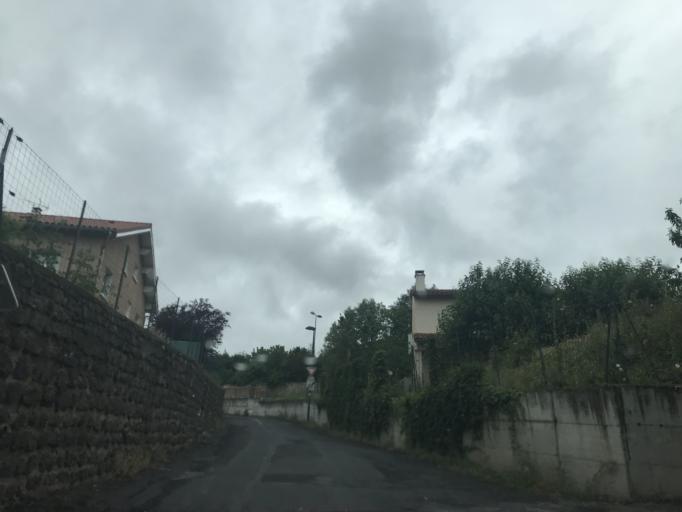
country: FR
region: Auvergne
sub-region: Departement de la Haute-Loire
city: Espaly-Saint-Marcel
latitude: 45.0583
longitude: 3.8777
